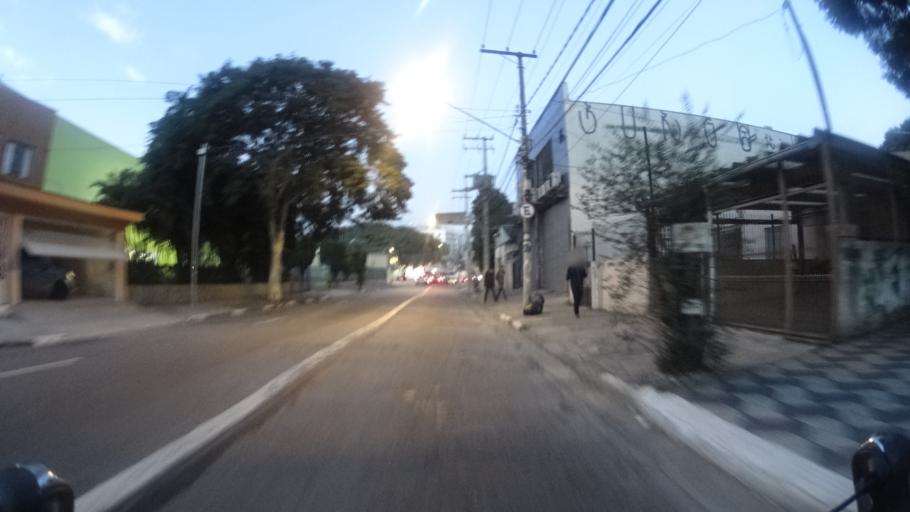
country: BR
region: Sao Paulo
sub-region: Sao Paulo
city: Sao Paulo
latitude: -23.5143
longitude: -46.6550
